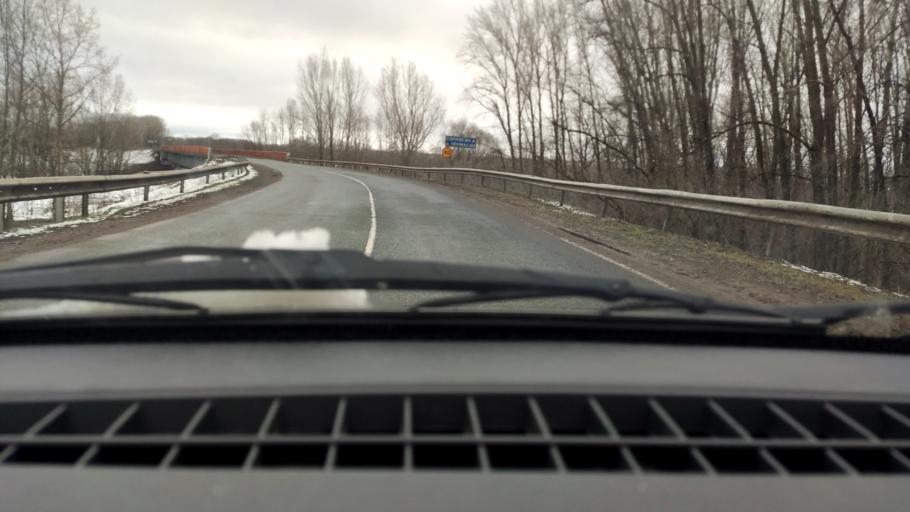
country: RU
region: Bashkortostan
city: Alekseyevka
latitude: 55.0794
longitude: 55.0676
